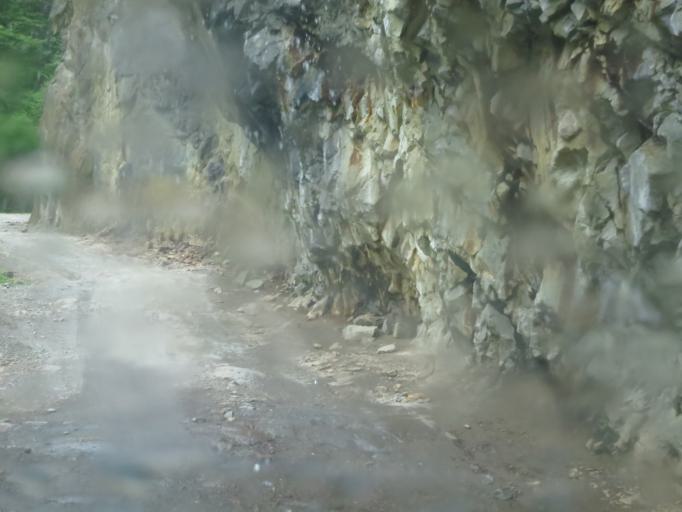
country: GE
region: Kakheti
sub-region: Telavi
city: Telavi
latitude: 42.2375
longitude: 45.4924
